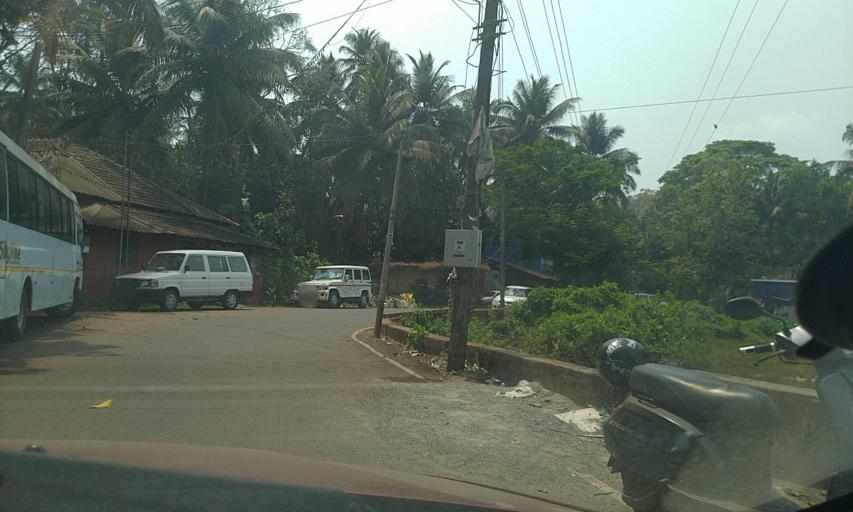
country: IN
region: Goa
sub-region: North Goa
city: Serula
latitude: 15.5207
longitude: 73.8415
